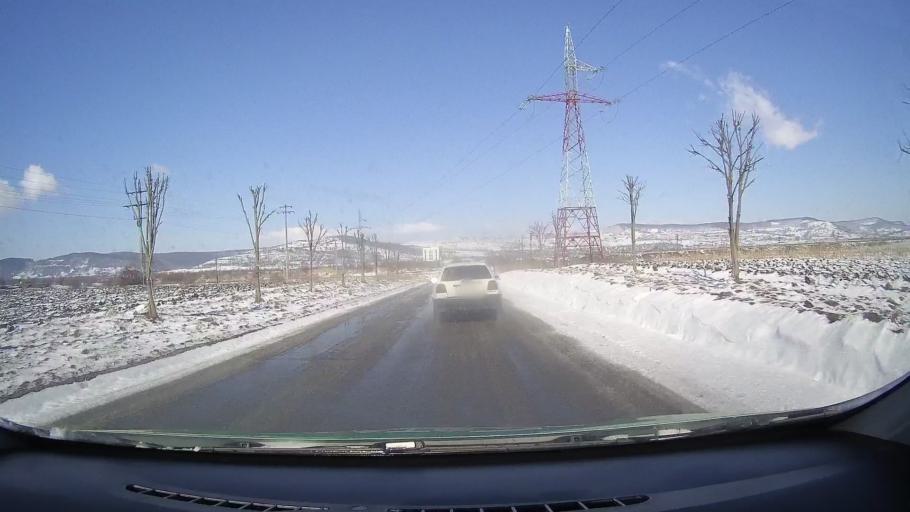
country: RO
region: Sibiu
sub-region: Comuna Avrig
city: Avrig
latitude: 45.7389
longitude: 24.3928
